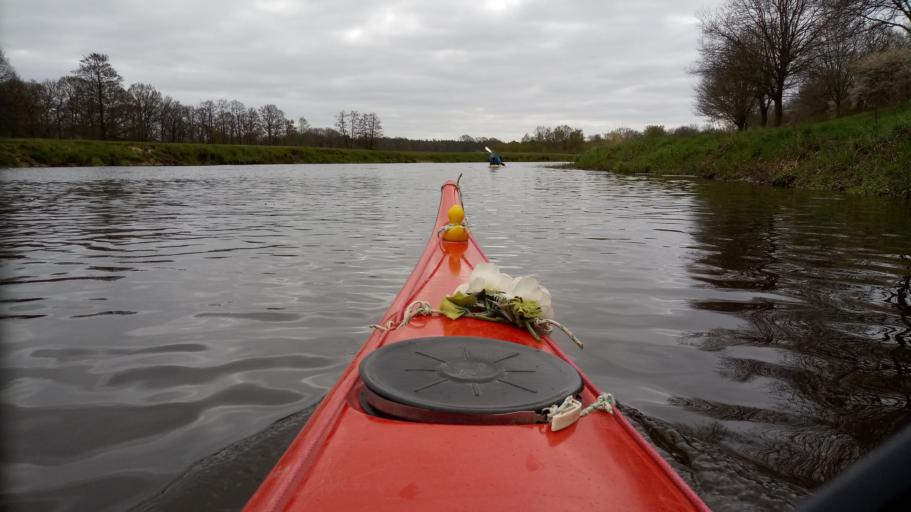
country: NL
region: Overijssel
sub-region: Gemeente Twenterand
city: Den Ham
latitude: 52.4941
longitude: 6.4170
